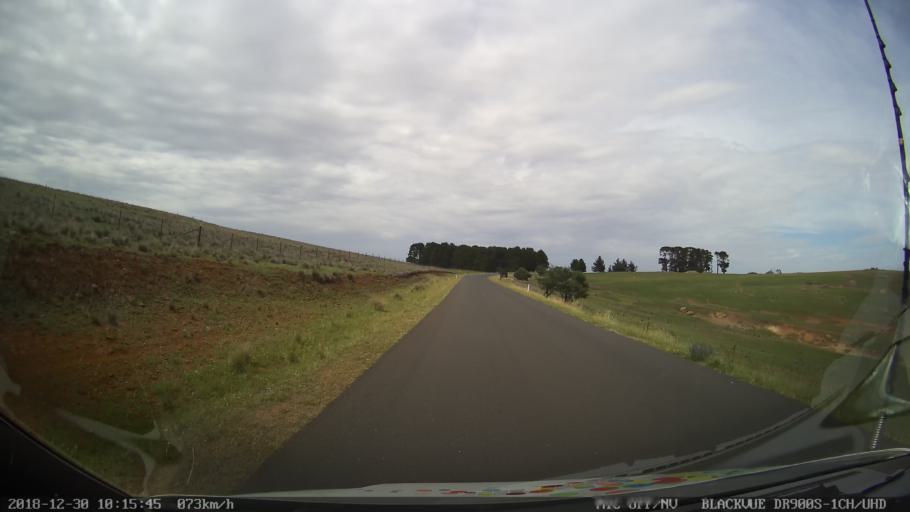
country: AU
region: New South Wales
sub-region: Snowy River
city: Berridale
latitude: -36.5448
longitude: 149.0433
